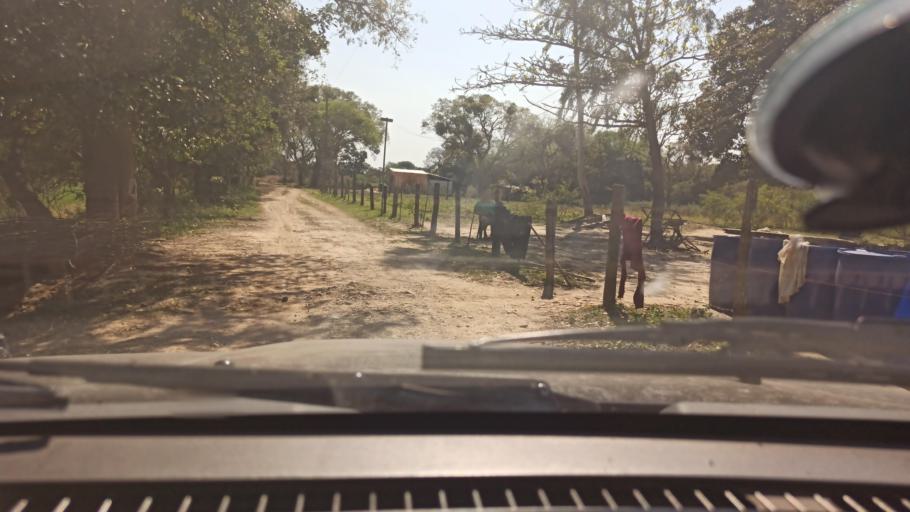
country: PY
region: Asuncion
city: Asuncion
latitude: -25.3346
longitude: -57.6811
